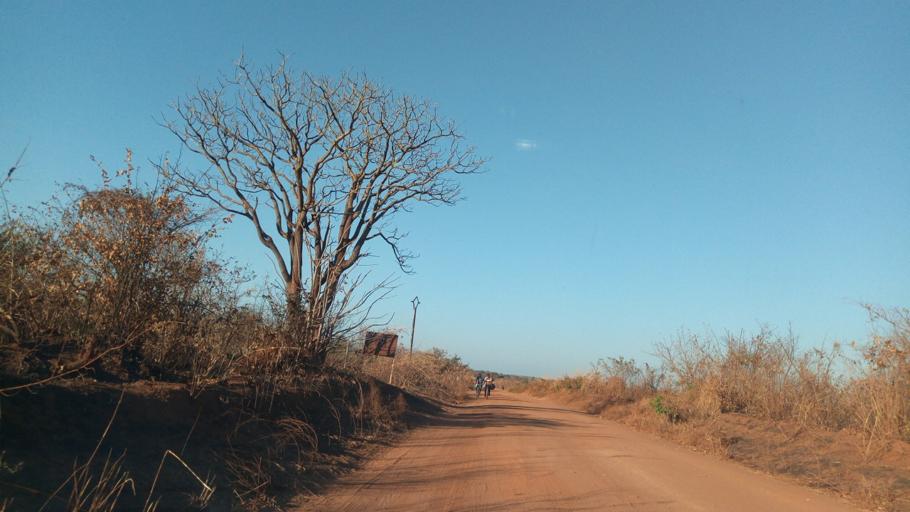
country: ZM
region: Luapula
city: Mwense
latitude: -10.4132
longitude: 28.6090
